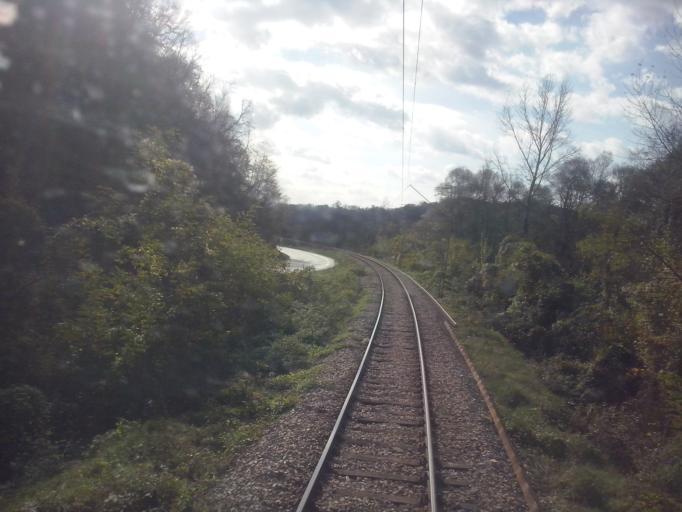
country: RS
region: Central Serbia
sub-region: Zlatiborski Okrug
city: Pozega
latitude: 43.8952
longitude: 19.9963
